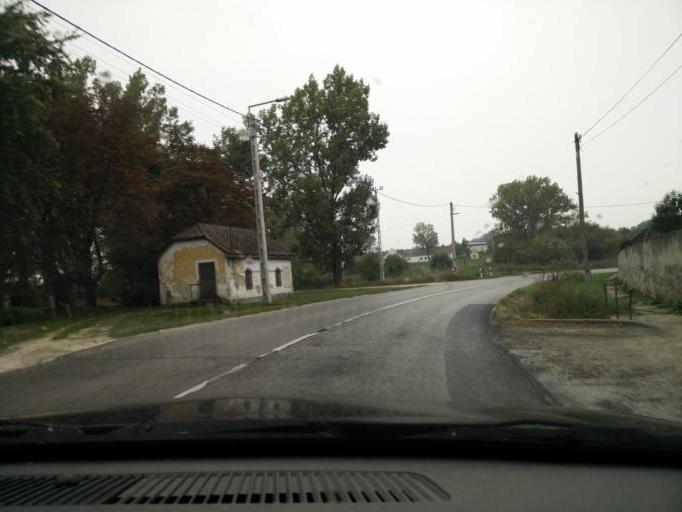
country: HU
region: Pest
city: Perbal
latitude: 47.6170
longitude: 18.7795
